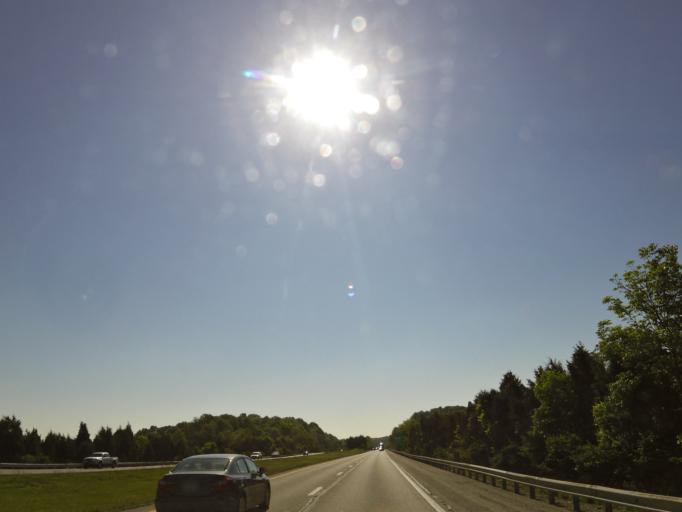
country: US
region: Kentucky
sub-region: Franklin County
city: Frankfort
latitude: 38.1465
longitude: -85.0136
